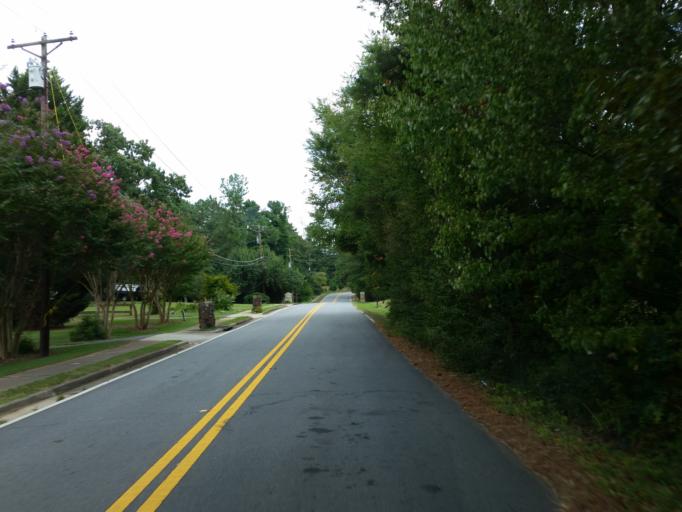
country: US
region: Georgia
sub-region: Cherokee County
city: Woodstock
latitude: 34.0482
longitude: -84.5067
